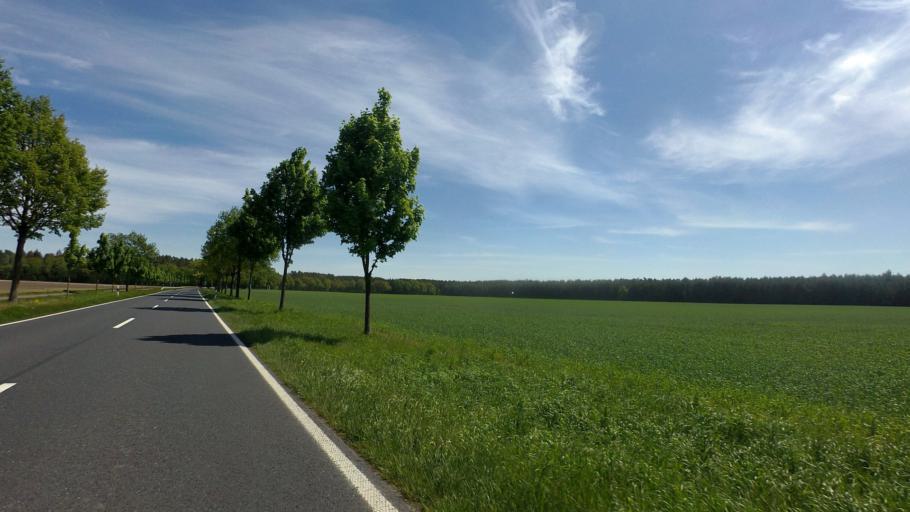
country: DE
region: Brandenburg
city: Luckenwalde
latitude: 52.0518
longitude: 13.2463
